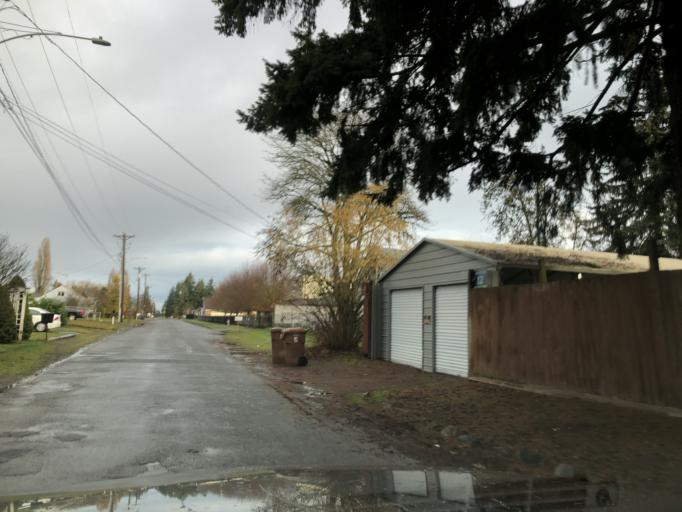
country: US
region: Washington
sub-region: Pierce County
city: Parkland
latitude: 47.1703
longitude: -122.4367
